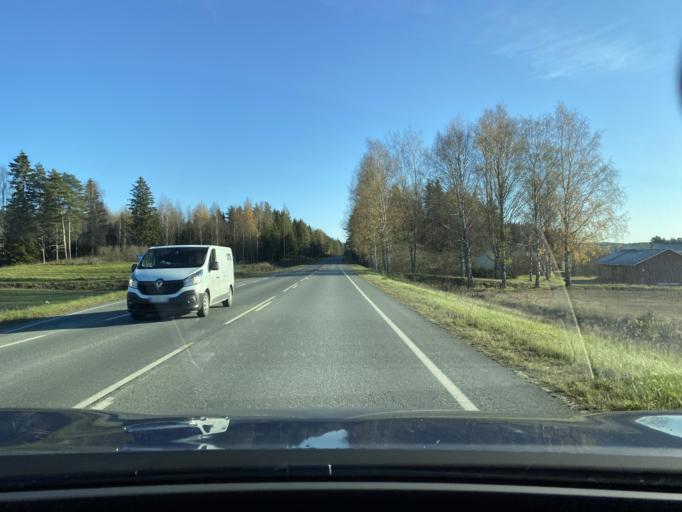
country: FI
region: Haeme
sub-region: Haemeenlinna
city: Parola
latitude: 61.0159
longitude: 24.3587
